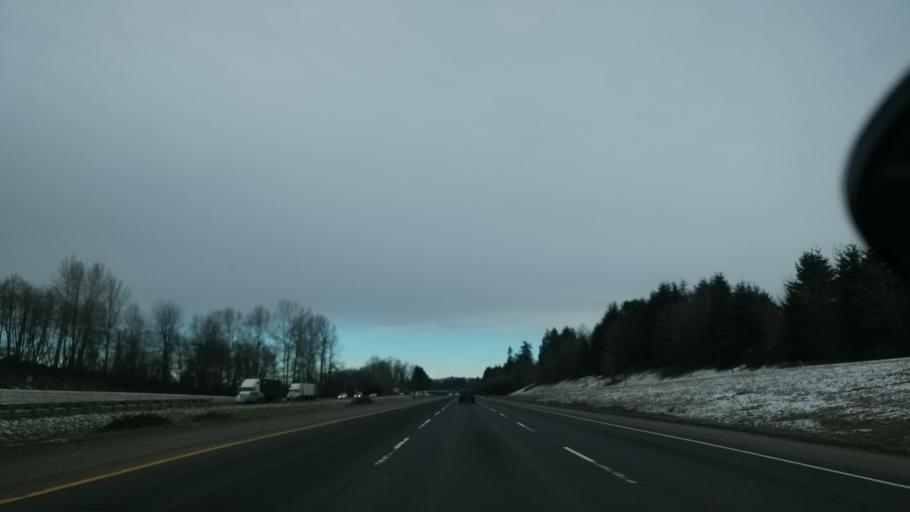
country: US
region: Washington
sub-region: Cowlitz County
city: West Side Highway
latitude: 46.1845
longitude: -122.8973
